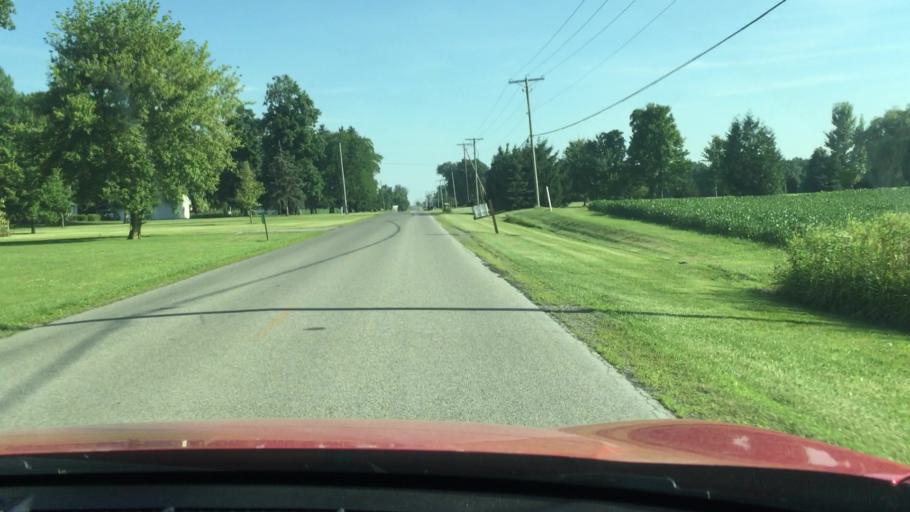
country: US
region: Ohio
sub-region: Hardin County
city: Ada
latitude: 40.7391
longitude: -83.8424
